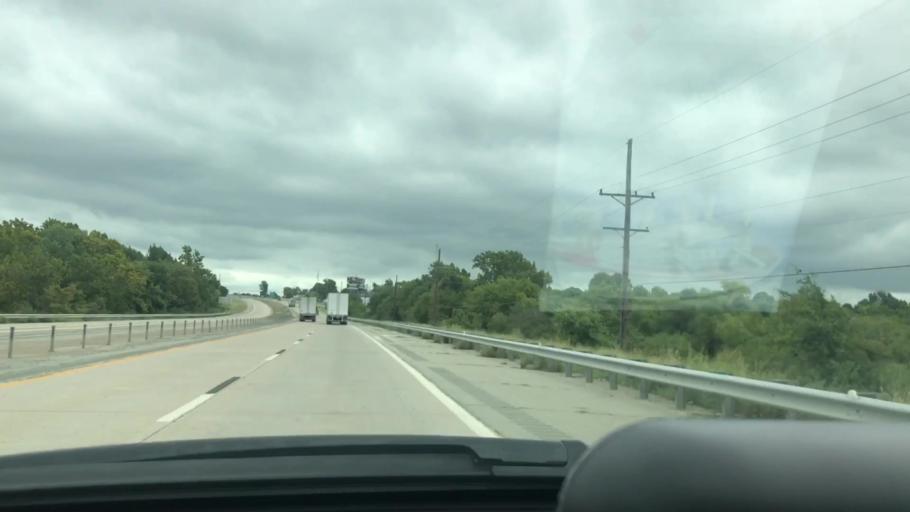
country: US
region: Oklahoma
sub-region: McIntosh County
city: Eufaula
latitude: 35.3501
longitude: -95.5785
